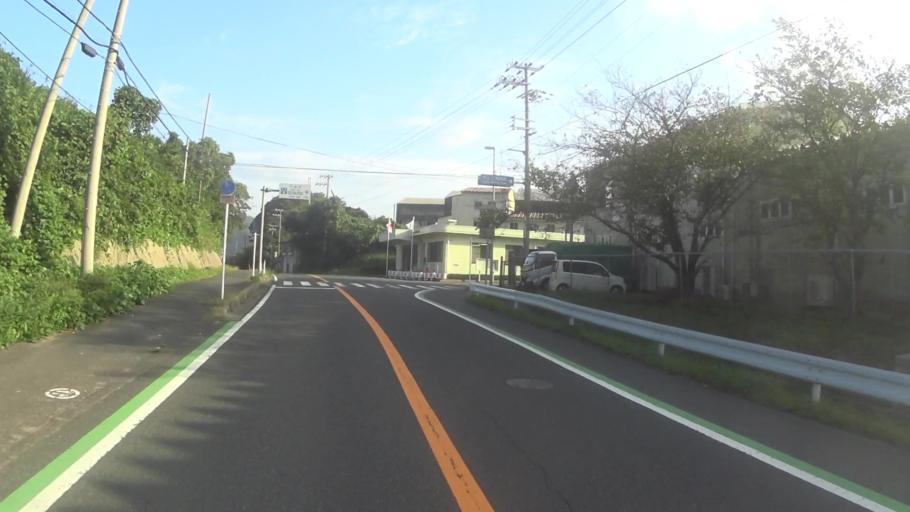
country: JP
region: Kyoto
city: Miyazu
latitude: 35.7225
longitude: 135.1018
